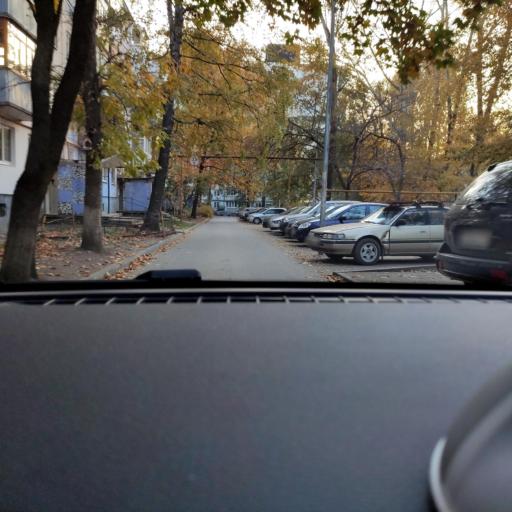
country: RU
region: Samara
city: Samara
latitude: 53.2424
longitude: 50.2480
